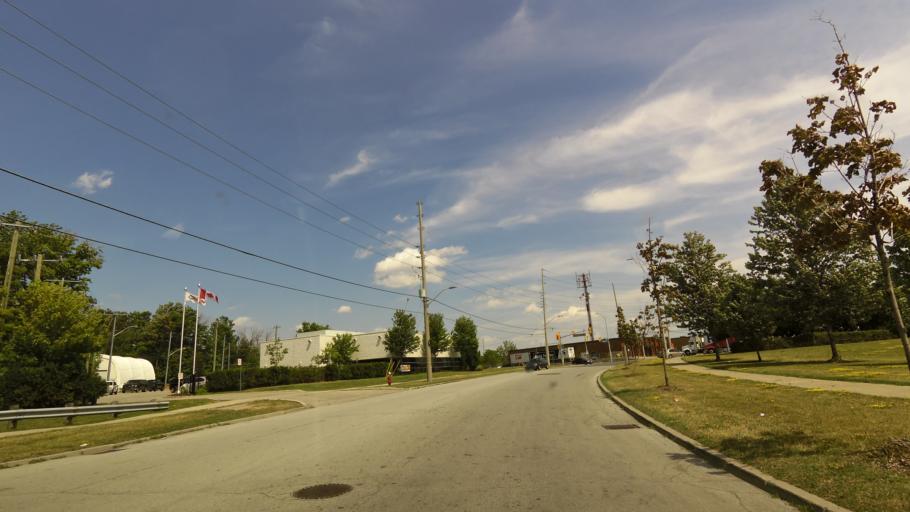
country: CA
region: Ontario
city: Etobicoke
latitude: 43.6488
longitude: -79.6224
